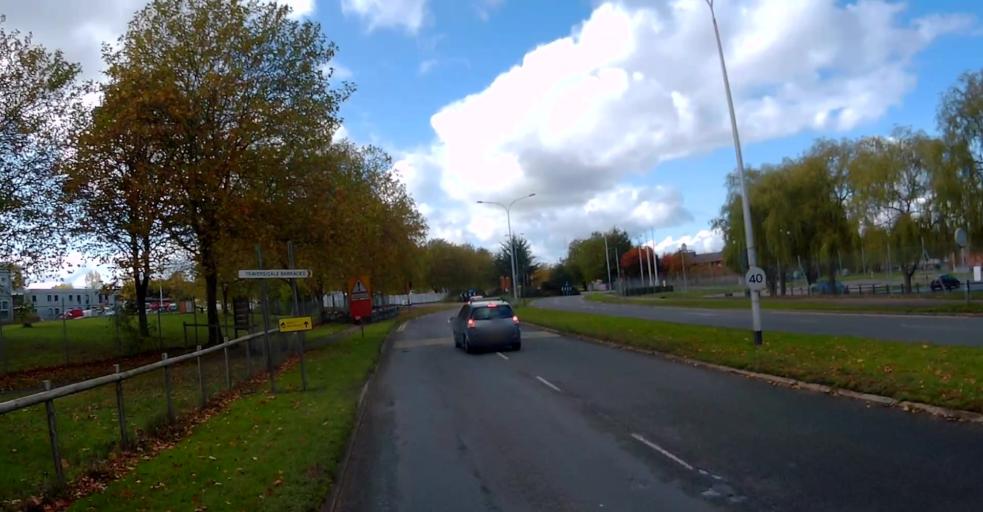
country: GB
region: England
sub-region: Hampshire
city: Aldershot
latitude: 51.2586
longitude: -0.7539
